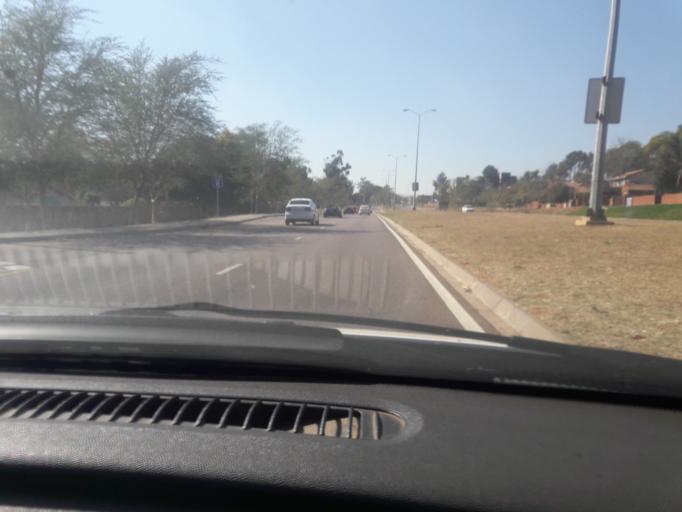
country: ZA
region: Gauteng
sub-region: City of Tshwane Metropolitan Municipality
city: Pretoria
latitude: -25.7660
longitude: 28.3085
